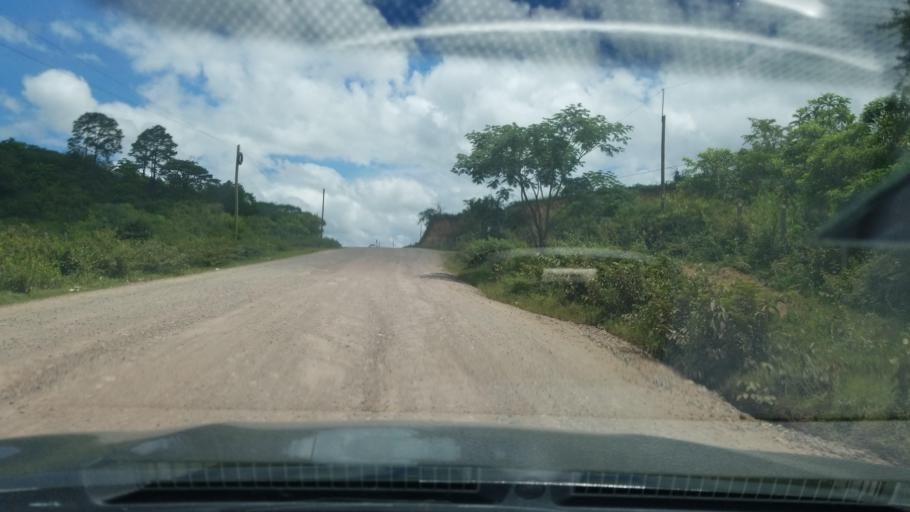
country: HN
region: Francisco Morazan
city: Talanga
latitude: 14.3845
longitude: -87.0704
